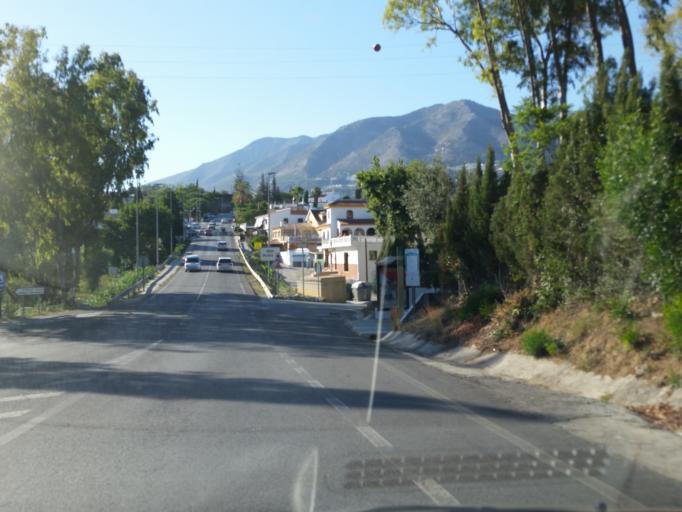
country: ES
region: Andalusia
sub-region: Provincia de Malaga
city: Fuengirola
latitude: 36.5669
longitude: -4.6301
